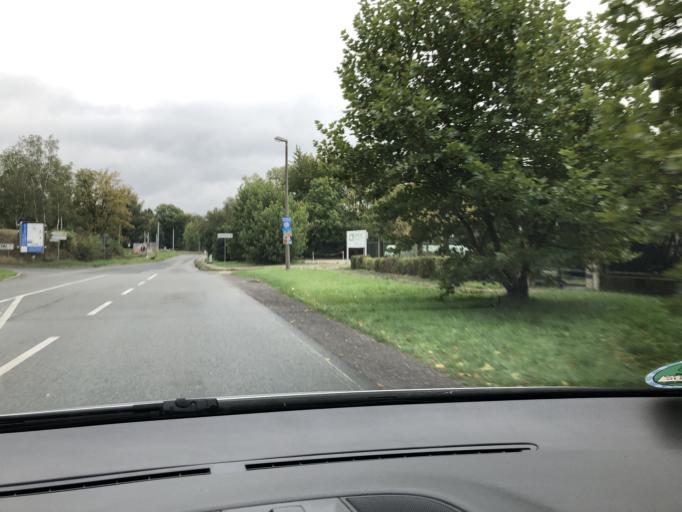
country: DE
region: Thuringia
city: Gera
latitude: 50.9061
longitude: 12.0698
